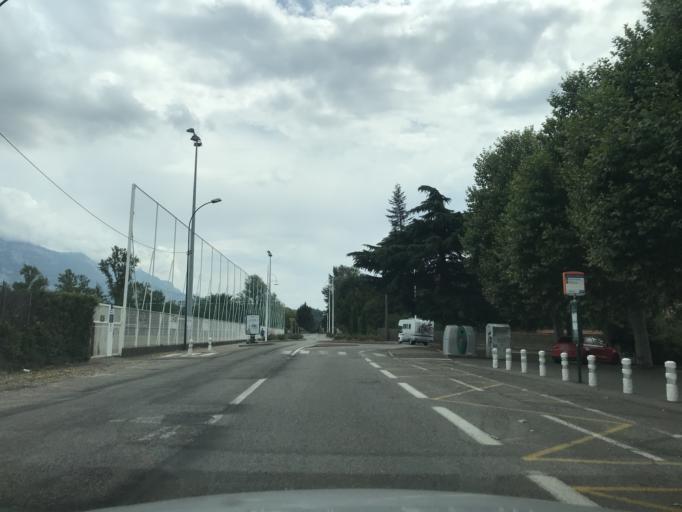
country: FR
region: Rhone-Alpes
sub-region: Departement de la Savoie
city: Brison-Saint-Innocent
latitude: 45.7028
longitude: 5.8913
